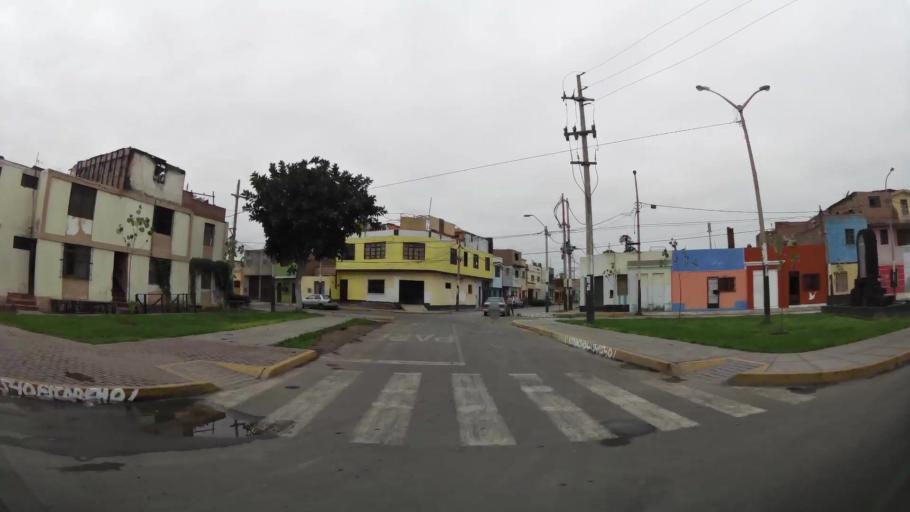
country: PE
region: Callao
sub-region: Callao
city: Callao
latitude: -12.0672
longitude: -77.1331
